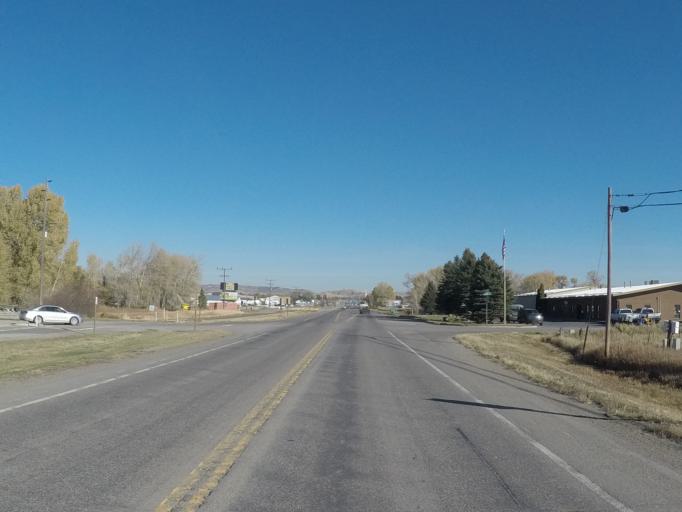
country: US
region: Montana
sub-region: Park County
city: Livingston
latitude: 45.6342
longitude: -110.5758
